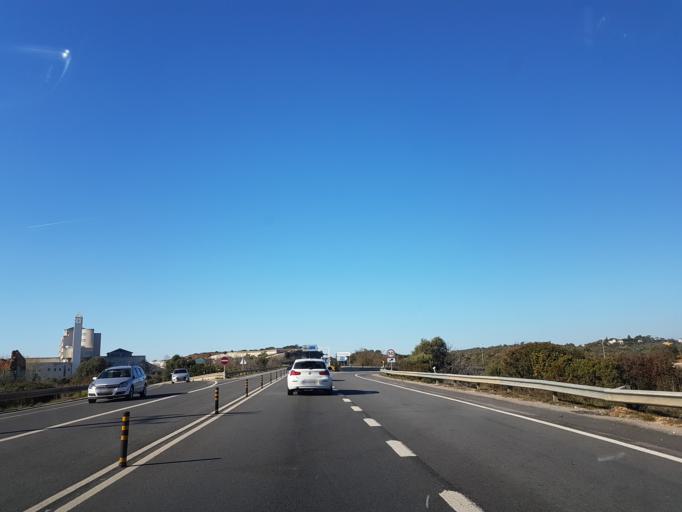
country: PT
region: Faro
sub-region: Portimao
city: Portimao
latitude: 37.1558
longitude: -8.5350
